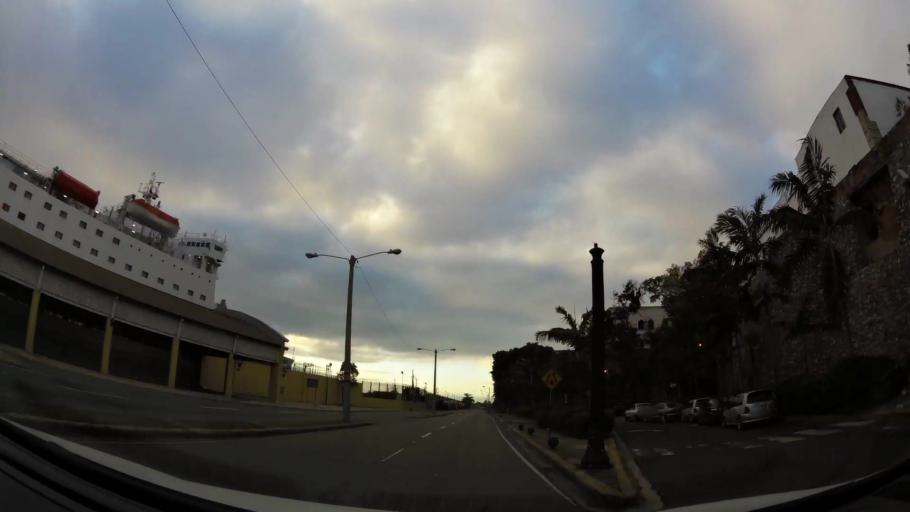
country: DO
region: Nacional
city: San Carlos
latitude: 18.4752
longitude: -69.8823
